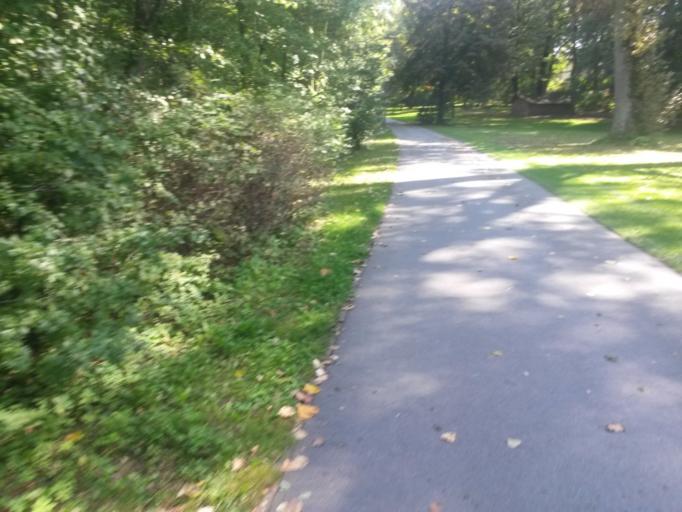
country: DE
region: Bavaria
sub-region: Regierungsbezirk Mittelfranken
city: Furth
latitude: 49.4735
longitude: 11.0003
